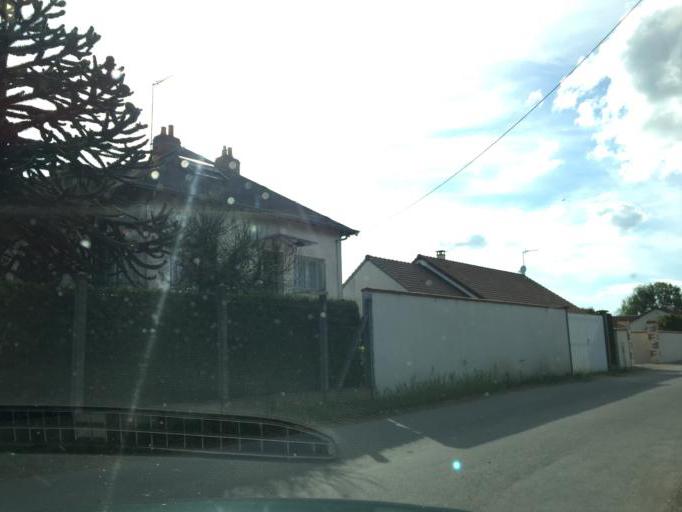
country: FR
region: Centre
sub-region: Departement du Loiret
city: Clery-Saint-Andre
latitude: 47.8323
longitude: 1.7713
